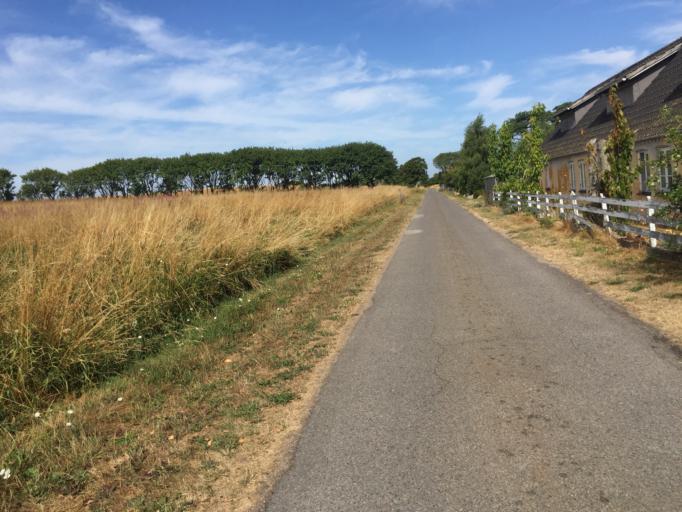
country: DK
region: Central Jutland
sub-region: Samso Kommune
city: Tranebjerg
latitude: 55.9537
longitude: 10.4242
